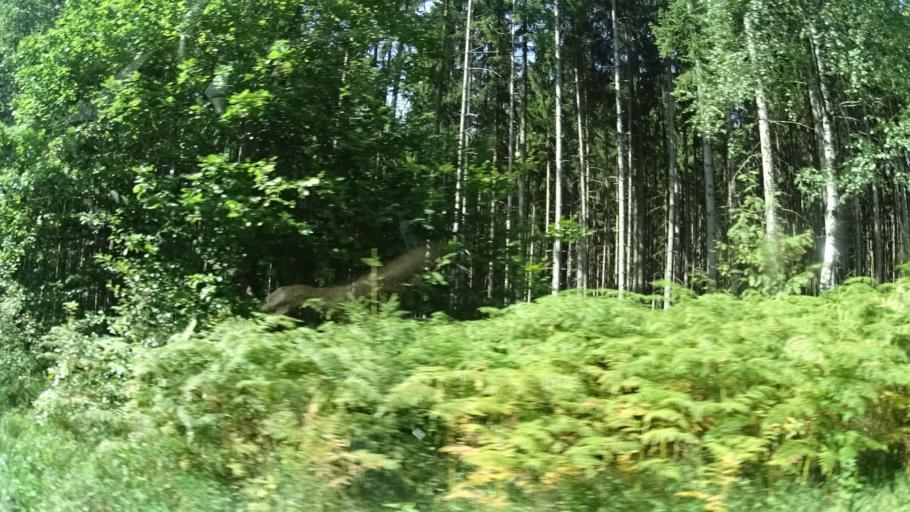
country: DE
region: Thuringia
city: Christes
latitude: 50.6480
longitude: 10.4673
